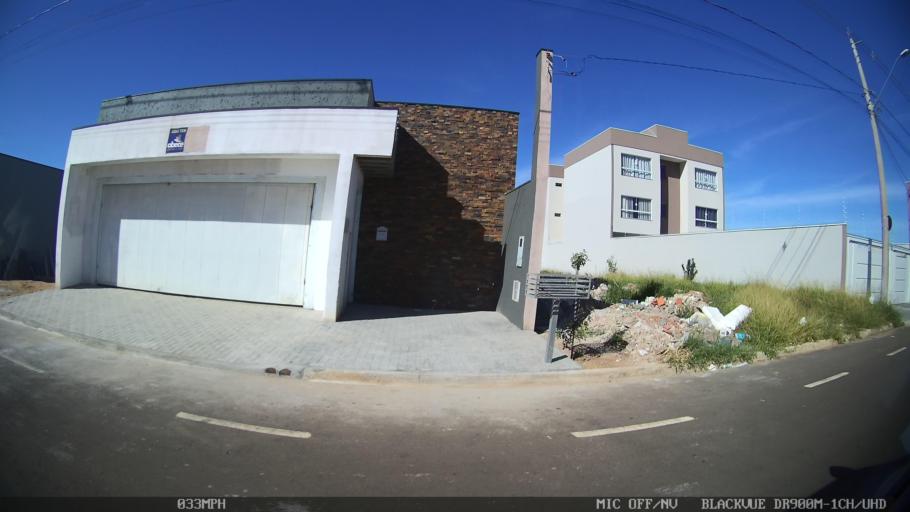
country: BR
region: Sao Paulo
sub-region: Franca
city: Franca
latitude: -20.5686
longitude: -47.3495
